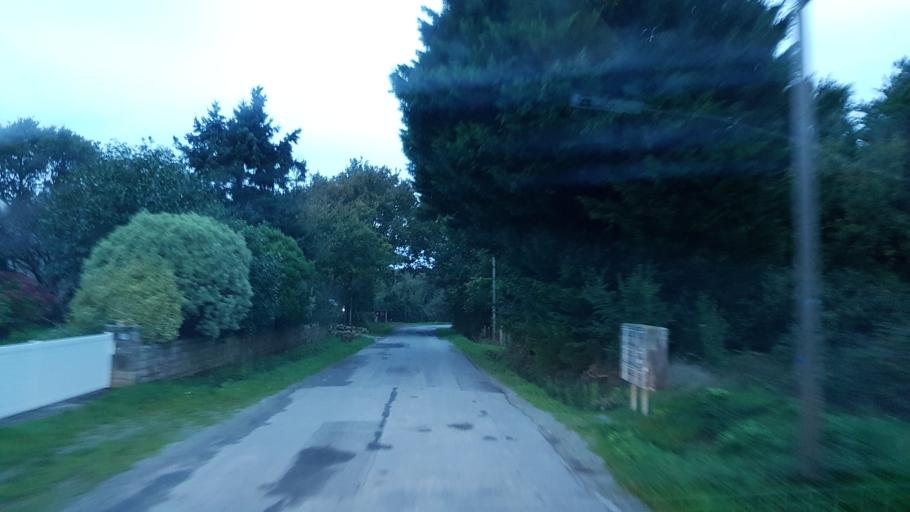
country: FR
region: Brittany
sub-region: Departement du Morbihan
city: Sarzeau
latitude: 47.5430
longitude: -2.8128
